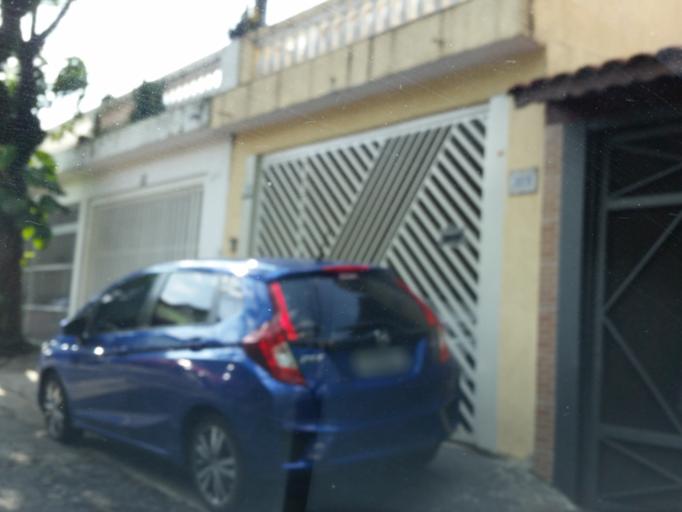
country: BR
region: Sao Paulo
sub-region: Diadema
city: Diadema
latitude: -23.6548
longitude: -46.6964
